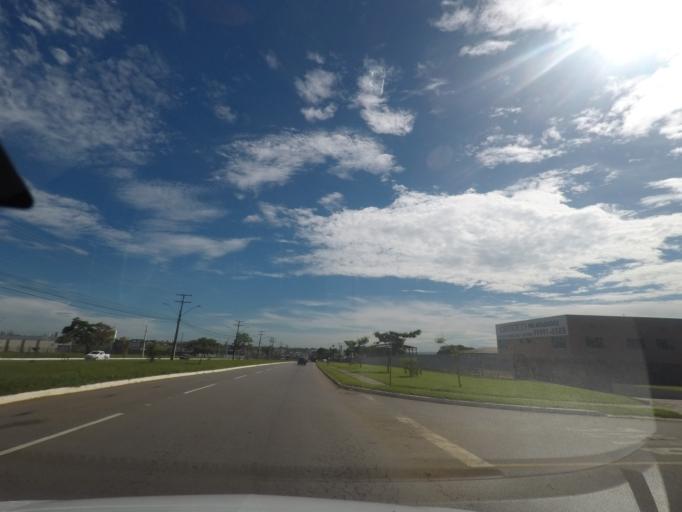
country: BR
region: Goias
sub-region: Aparecida De Goiania
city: Aparecida de Goiania
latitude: -16.7913
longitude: -49.2527
